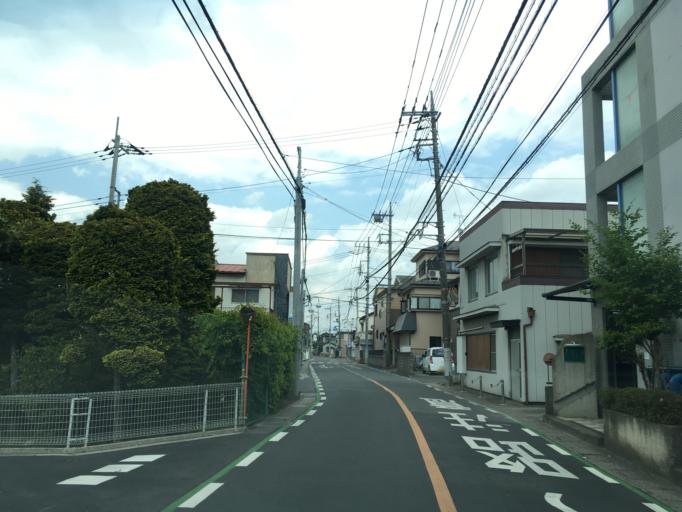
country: JP
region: Saitama
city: Sayama
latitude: 35.8610
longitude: 139.4129
